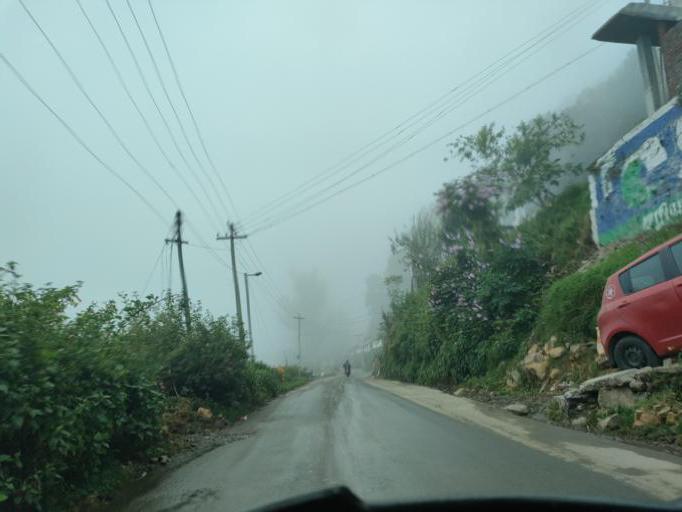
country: IN
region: Tamil Nadu
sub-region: Dindigul
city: Kodaikanal
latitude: 10.2340
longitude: 77.4767
